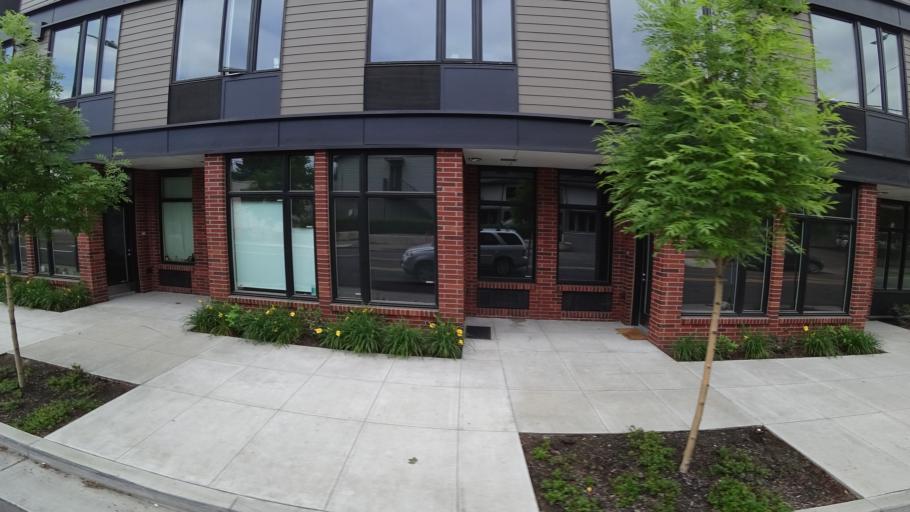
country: US
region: Oregon
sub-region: Multnomah County
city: Lents
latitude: 45.5059
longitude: -122.6112
